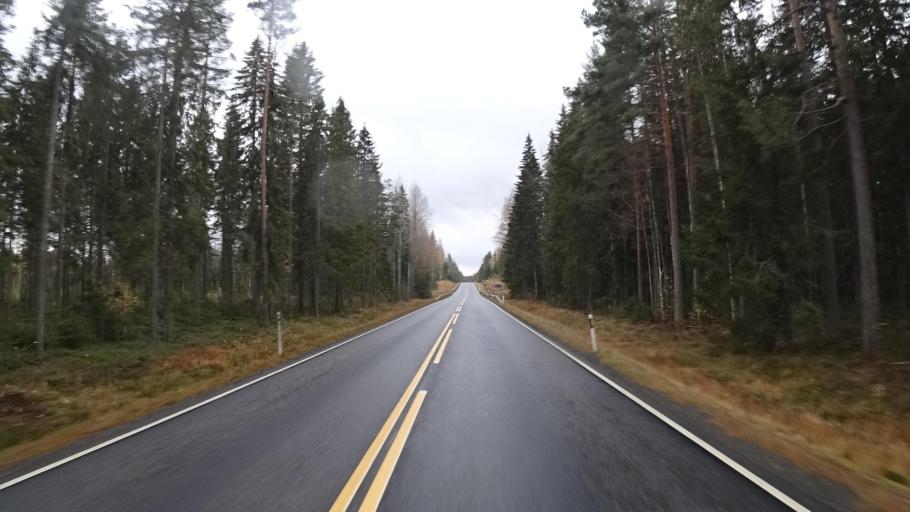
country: FI
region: Southern Savonia
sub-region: Mikkeli
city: Kangasniemi
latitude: 62.1571
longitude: 26.8240
